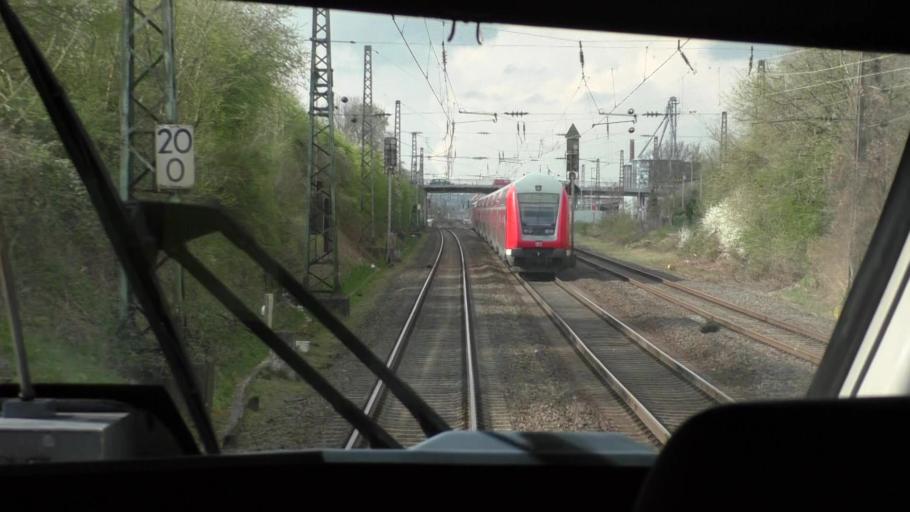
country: DE
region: North Rhine-Westphalia
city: Wesseling
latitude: 50.7915
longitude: 6.9631
